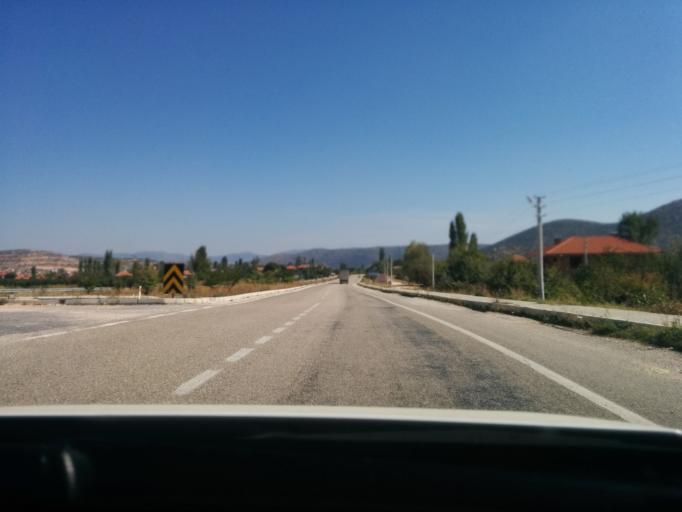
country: TR
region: Antalya
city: Korkuteli
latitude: 37.0509
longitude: 30.1957
